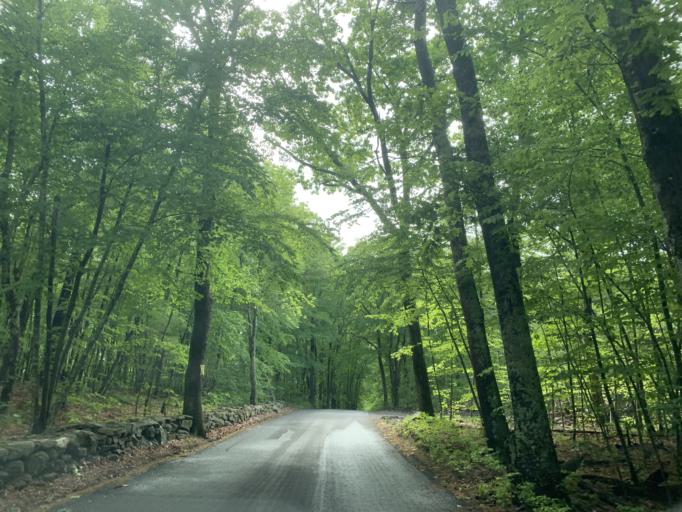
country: US
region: Massachusetts
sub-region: Worcester County
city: Upton
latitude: 42.2013
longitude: -71.6392
